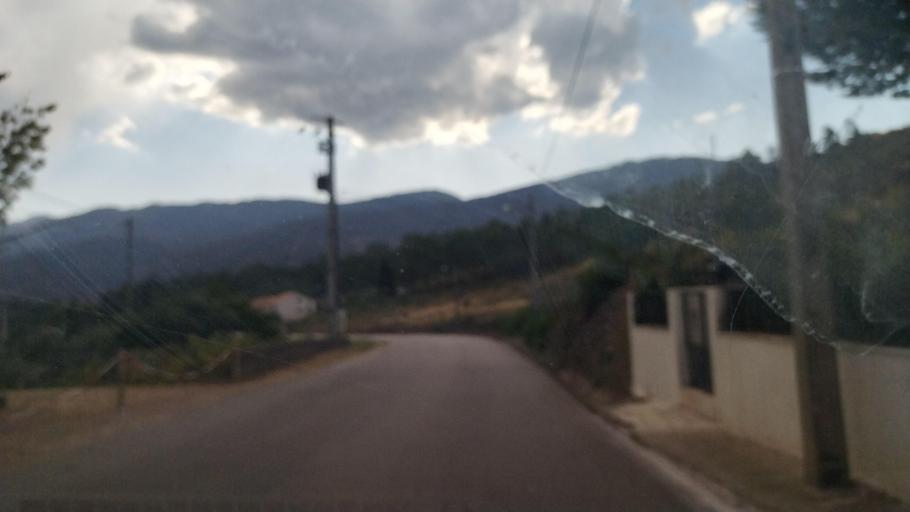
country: PT
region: Castelo Branco
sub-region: Covilha
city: Teixoso
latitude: 40.3795
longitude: -7.4567
